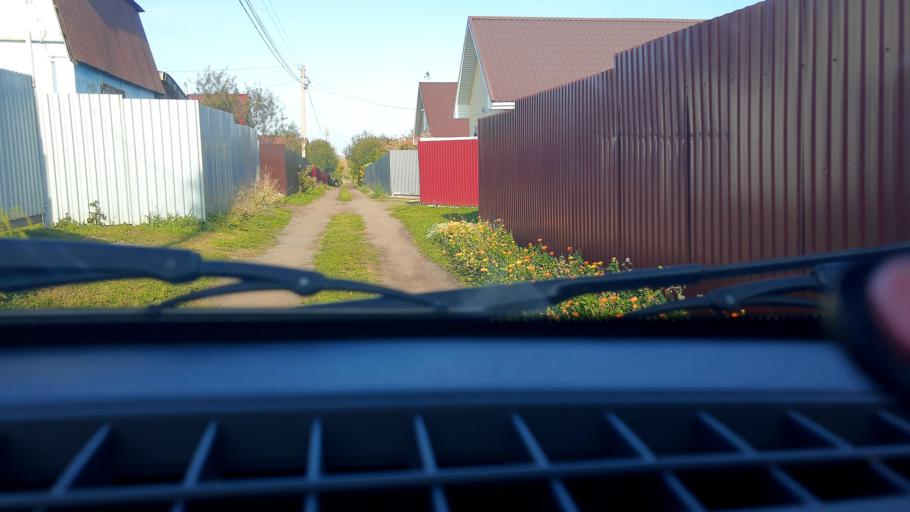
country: RU
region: Bashkortostan
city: Avdon
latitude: 54.5733
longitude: 55.7307
